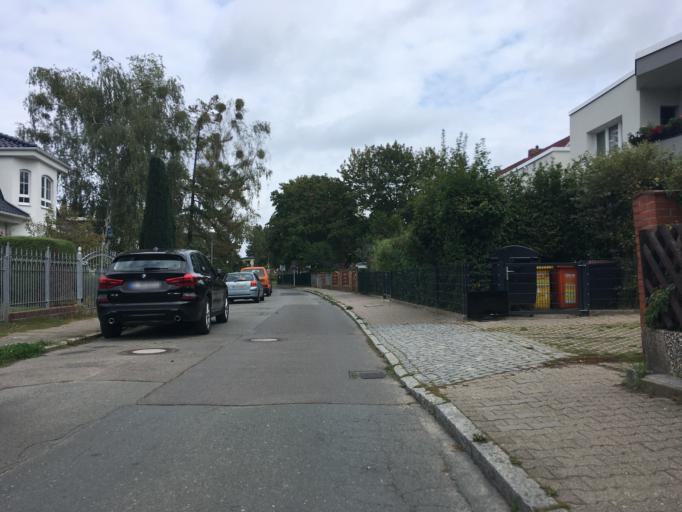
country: DE
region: Berlin
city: Lankwitz
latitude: 52.4168
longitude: 13.3317
